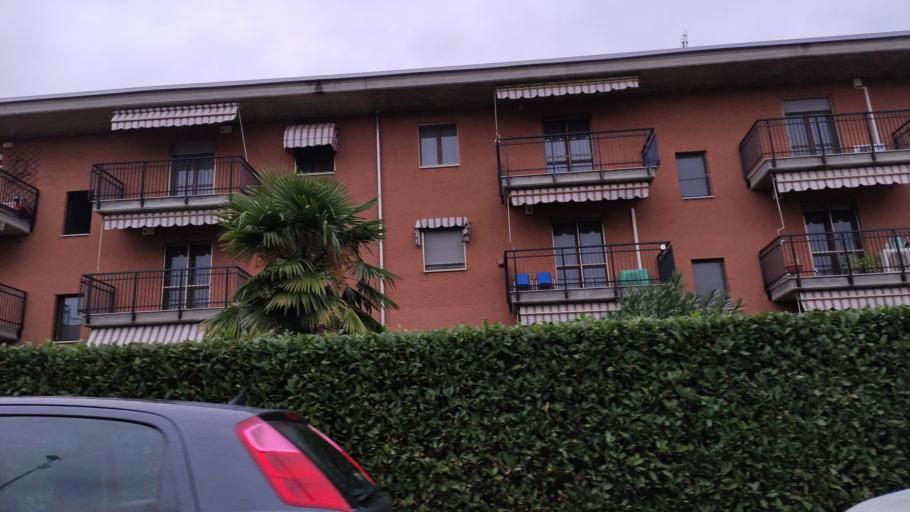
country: IT
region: Piedmont
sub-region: Provincia di Torino
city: Settimo Torinese
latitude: 45.1372
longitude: 7.7518
